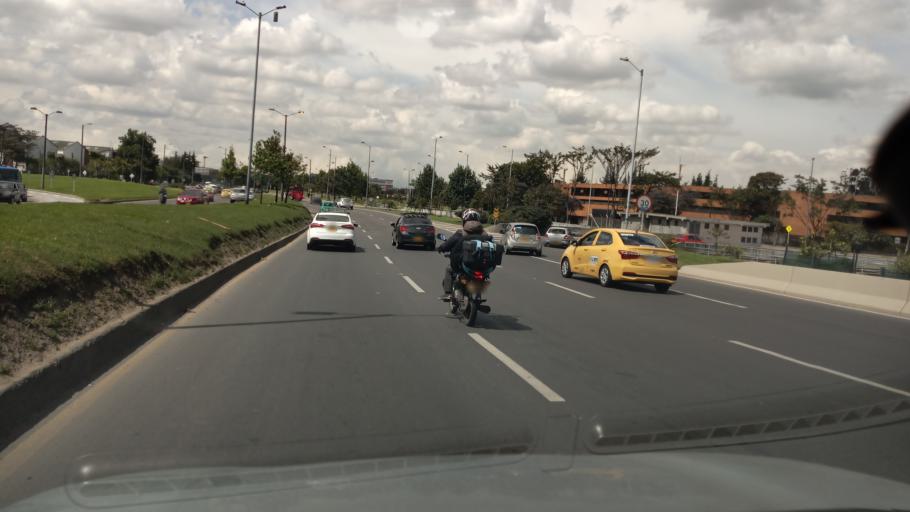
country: CO
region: Bogota D.C.
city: Bogota
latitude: 4.6781
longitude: -74.1205
